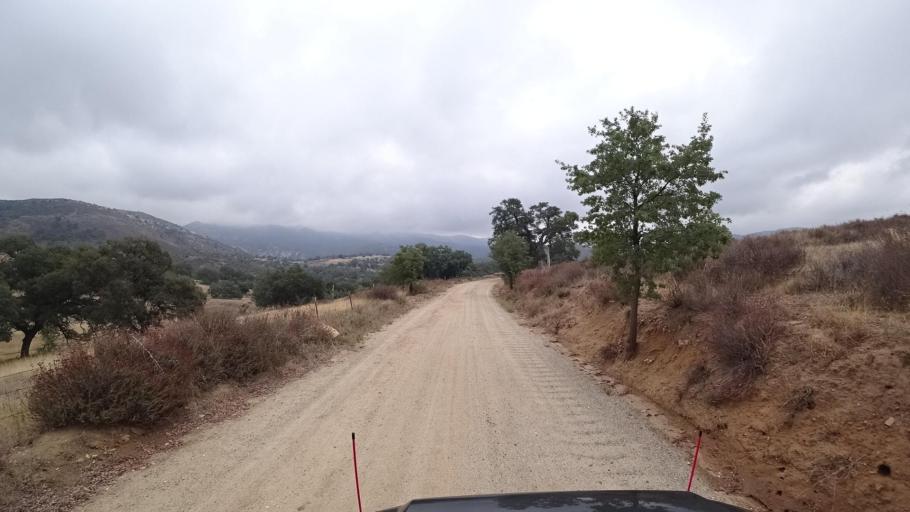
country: US
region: California
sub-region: San Diego County
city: Julian
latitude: 32.9867
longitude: -116.6597
